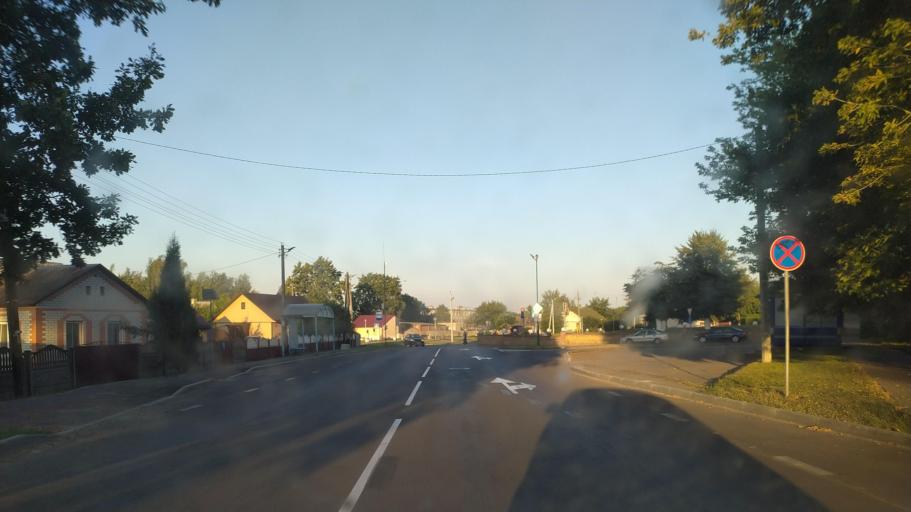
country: BY
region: Brest
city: Byaroza
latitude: 52.5394
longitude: 24.9849
